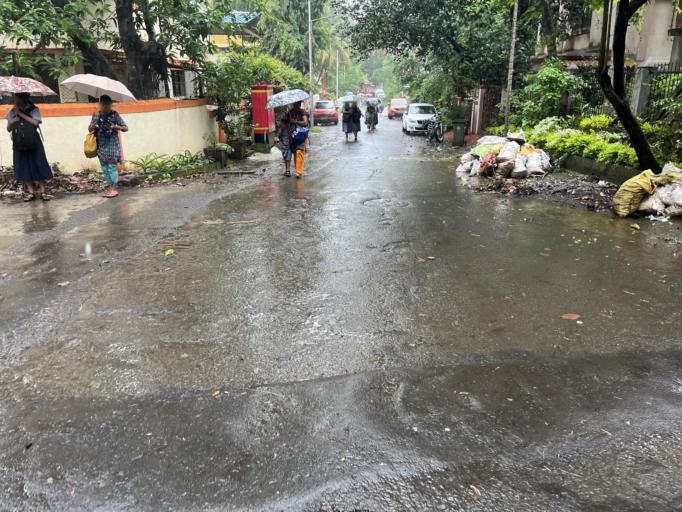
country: IN
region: Maharashtra
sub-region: Mumbai Suburban
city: Borivli
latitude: 19.2313
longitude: 72.8705
